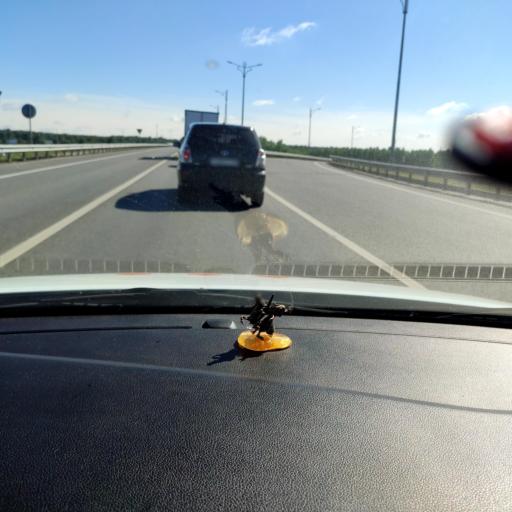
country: RU
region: Tatarstan
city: Stolbishchi
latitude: 55.6981
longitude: 49.2237
